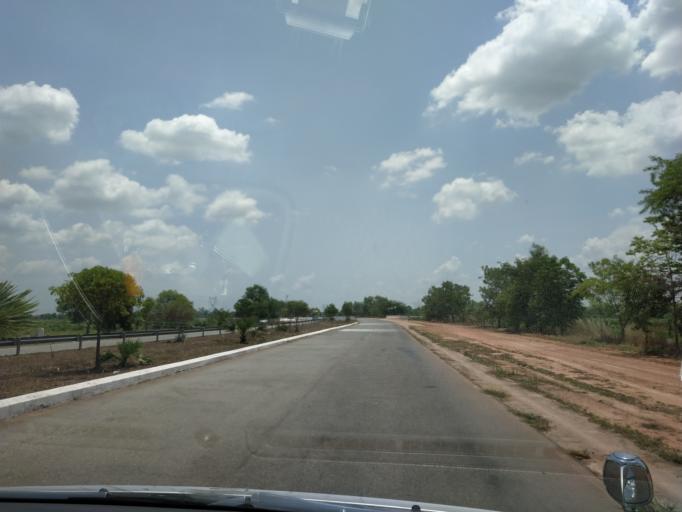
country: MM
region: Bago
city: Thanatpin
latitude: 17.2364
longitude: 96.2270
